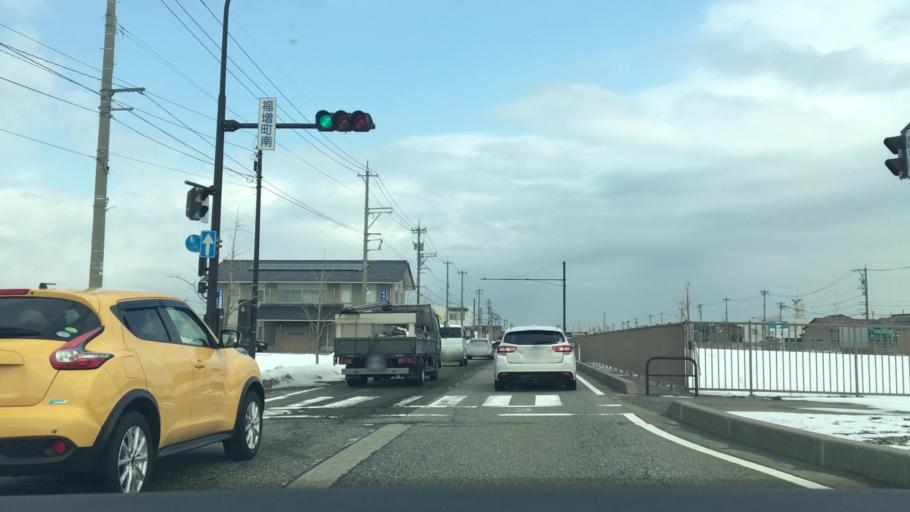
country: JP
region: Ishikawa
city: Matsuto
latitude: 36.5600
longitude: 136.5794
